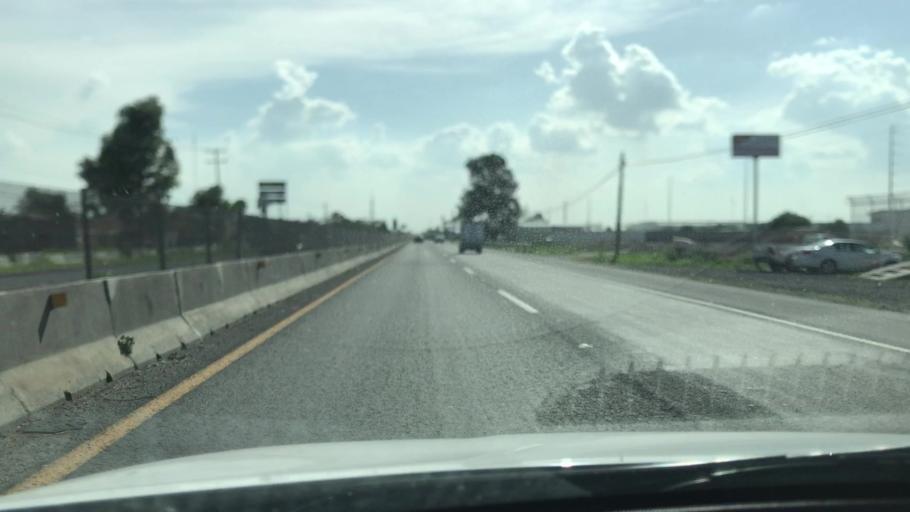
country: MX
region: Guanajuato
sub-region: Cortazar
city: Colonia la Calzada (La Olla)
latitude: 20.5122
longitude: -100.9403
